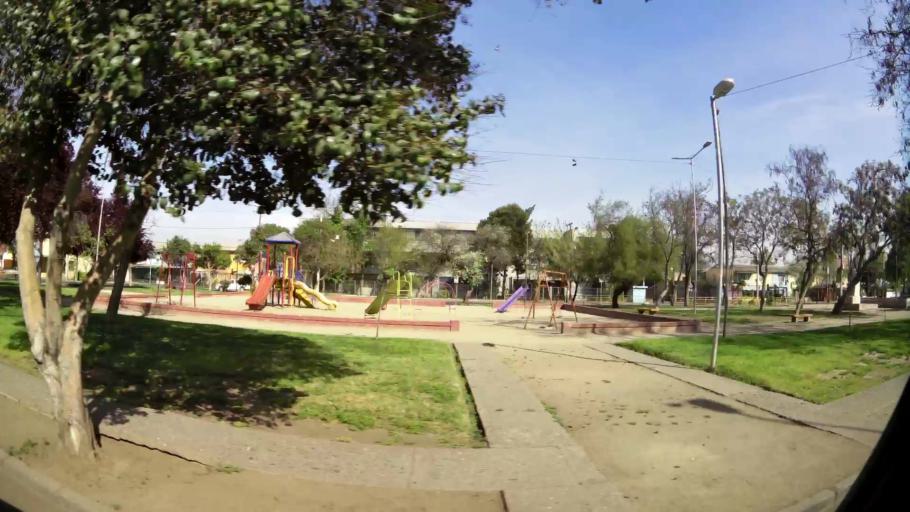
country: CL
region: Santiago Metropolitan
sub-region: Provincia de Santiago
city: Lo Prado
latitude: -33.4340
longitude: -70.7375
